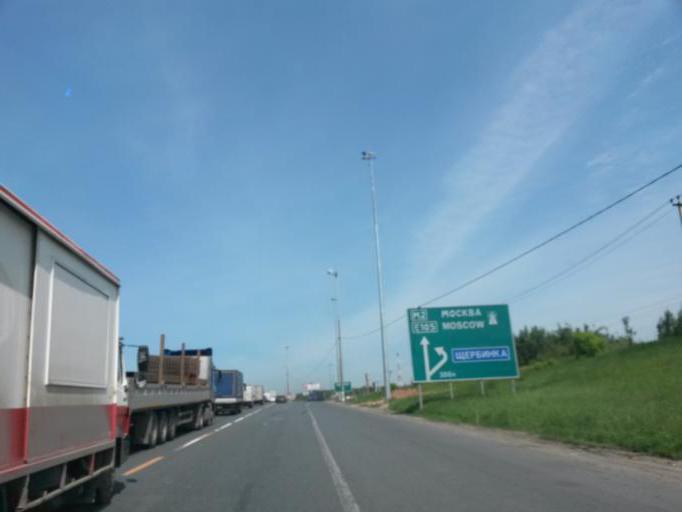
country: RU
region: Moskovskaya
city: Shcherbinka
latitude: 55.4769
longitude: 37.6164
